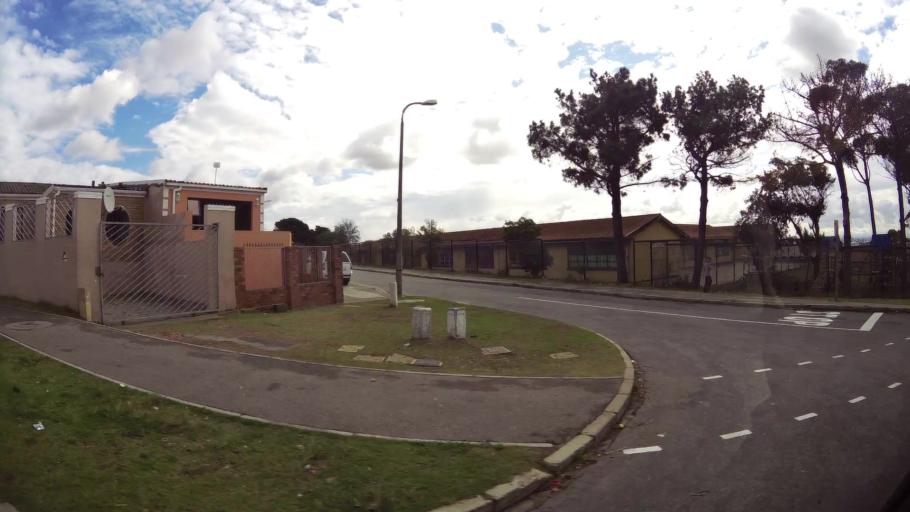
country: ZA
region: Eastern Cape
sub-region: Nelson Mandela Bay Metropolitan Municipality
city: Port Elizabeth
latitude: -33.9336
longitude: 25.5648
